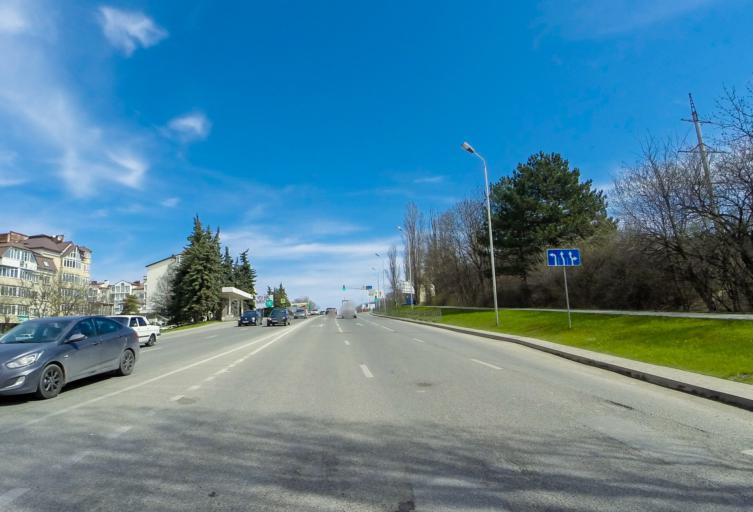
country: RU
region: Stavropol'skiy
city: Pyatigorsk
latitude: 44.0577
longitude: 43.0687
